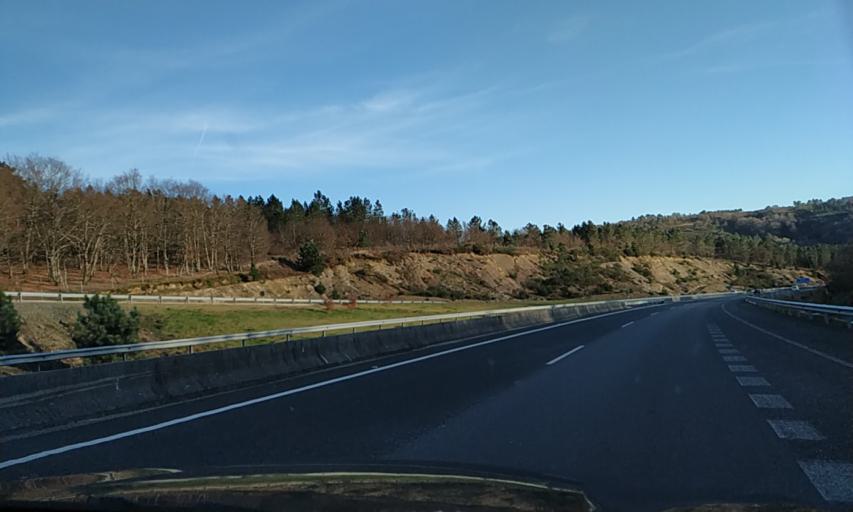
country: ES
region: Galicia
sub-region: Provincia de Pontevedra
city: Lalin
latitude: 42.6200
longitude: -8.0987
